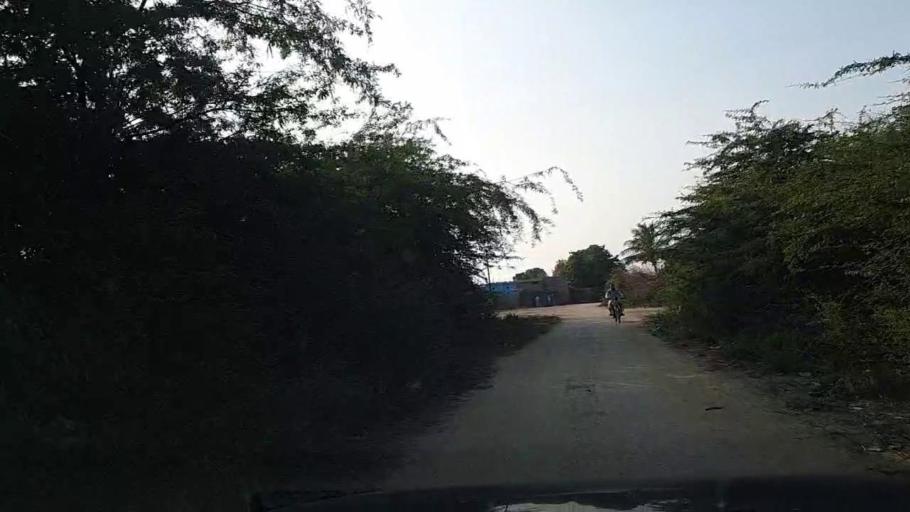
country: PK
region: Sindh
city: Gharo
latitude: 24.7781
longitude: 67.5074
